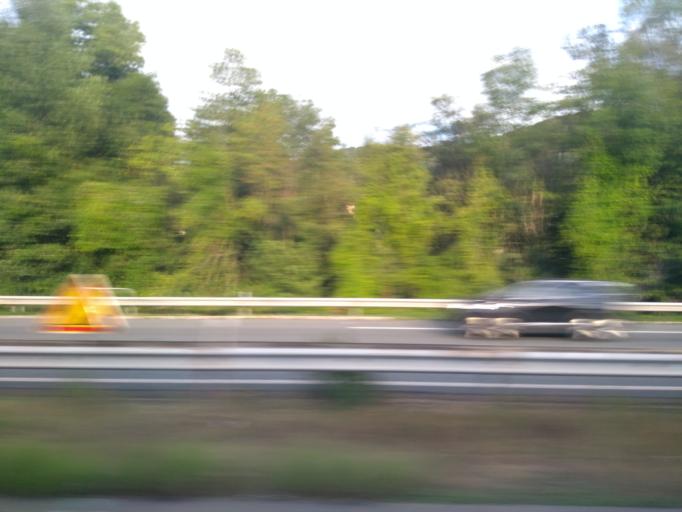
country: FR
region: Rhone-Alpes
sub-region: Departement de l'Isere
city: Chabons
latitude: 45.4786
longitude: 5.3984
